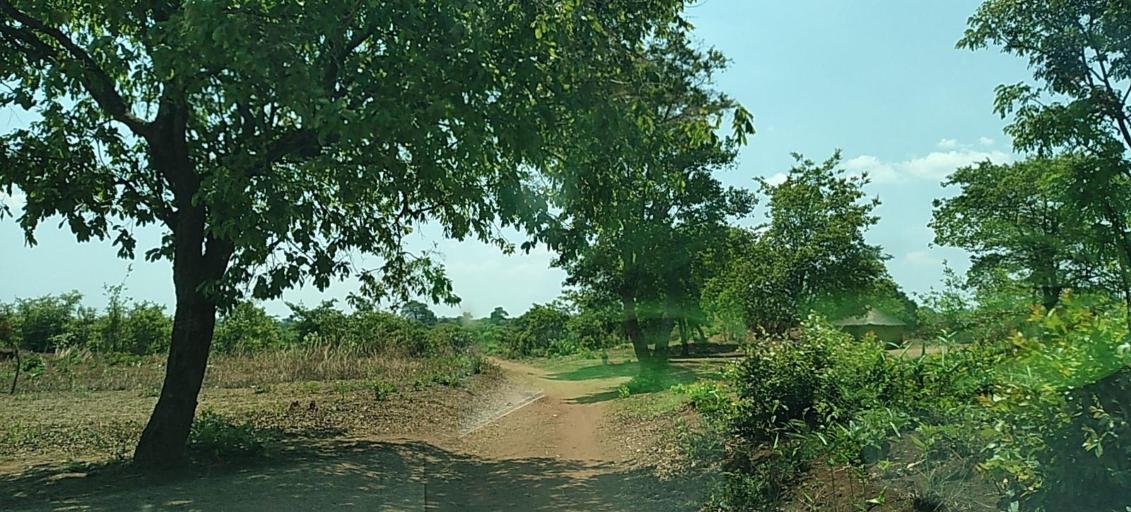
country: CD
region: Katanga
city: Kolwezi
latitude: -11.2914
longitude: 25.2065
